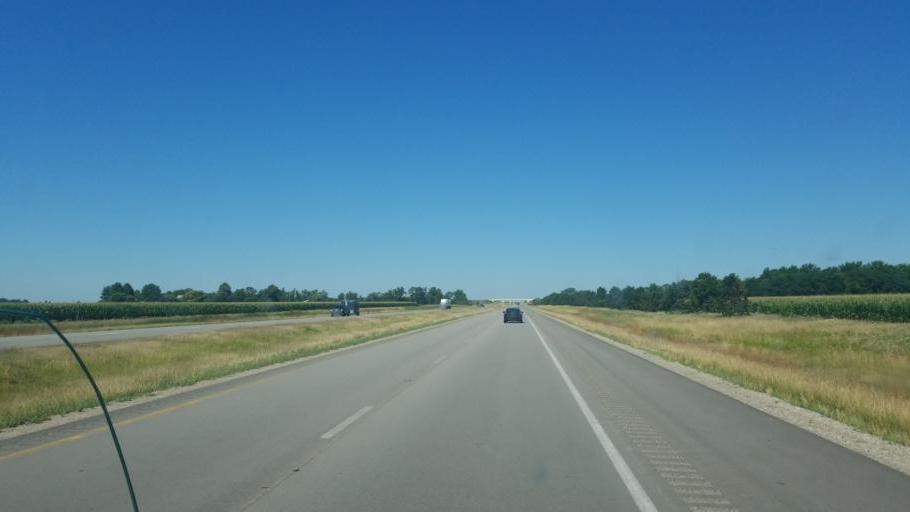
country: US
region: Ohio
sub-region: Allen County
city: Delphos
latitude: 40.8699
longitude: -84.4602
